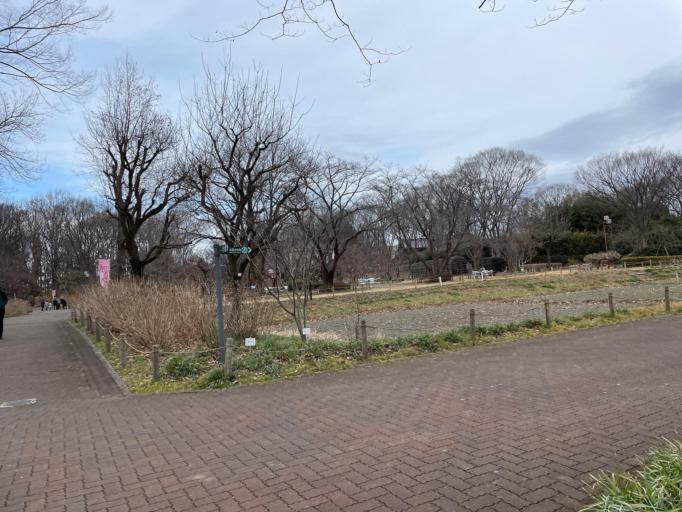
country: JP
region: Tokyo
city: Kokubunji
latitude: 35.6542
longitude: 139.4719
